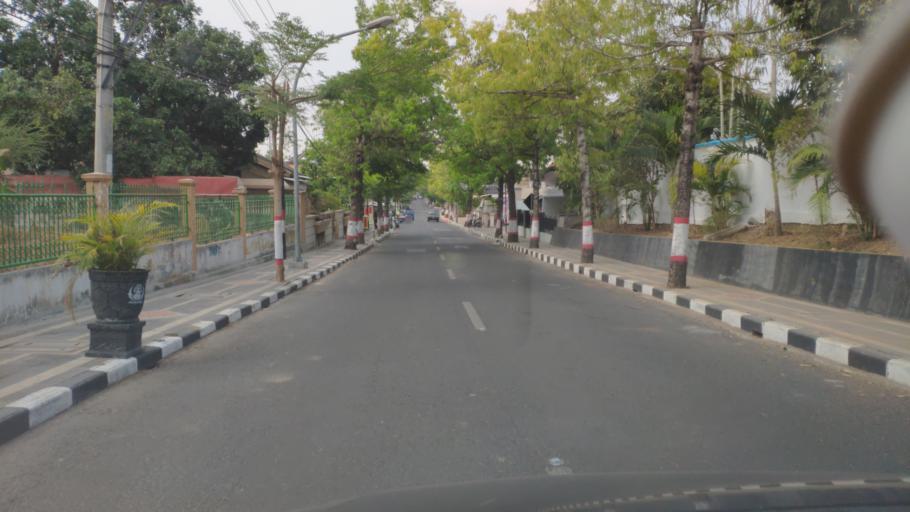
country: ID
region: Central Java
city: Tempelan
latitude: -6.9676
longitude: 111.4128
